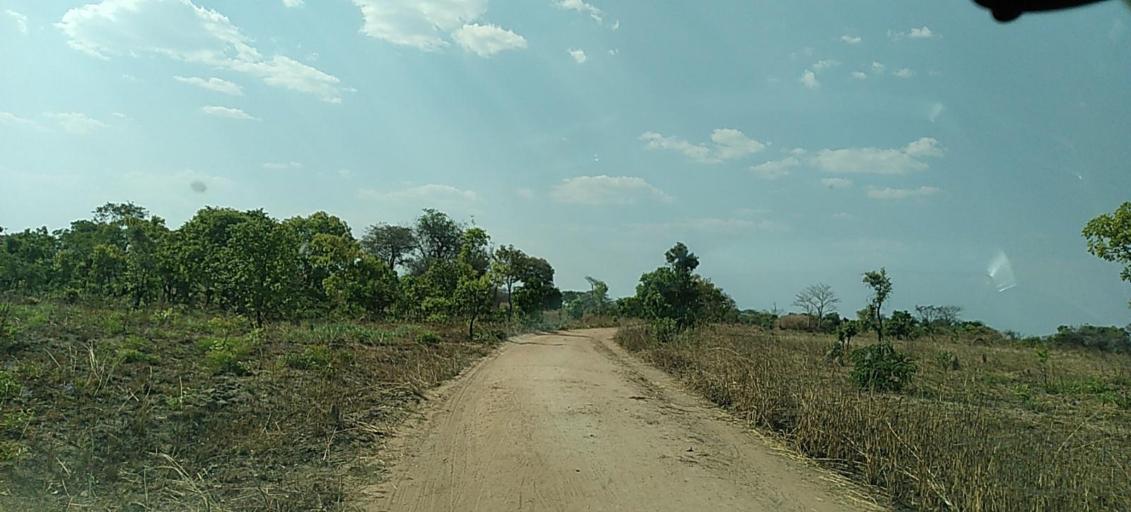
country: ZM
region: North-Western
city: Kalengwa
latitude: -13.1116
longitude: 24.9925
